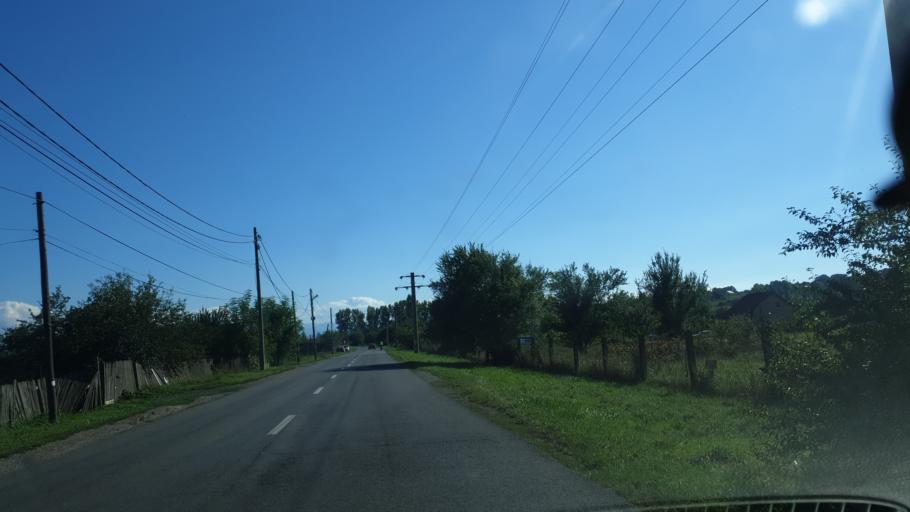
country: RO
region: Covasna
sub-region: Municipiul Sfantu Gheorghe
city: Sfantu-Gheorghe
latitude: 45.8422
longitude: 25.7765
